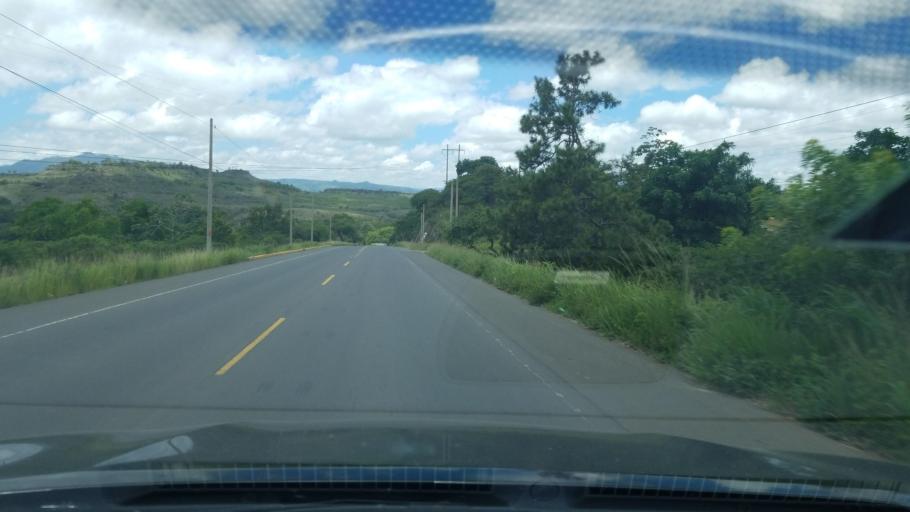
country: HN
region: Francisco Morazan
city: Cofradia
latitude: 14.3126
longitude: -87.2156
